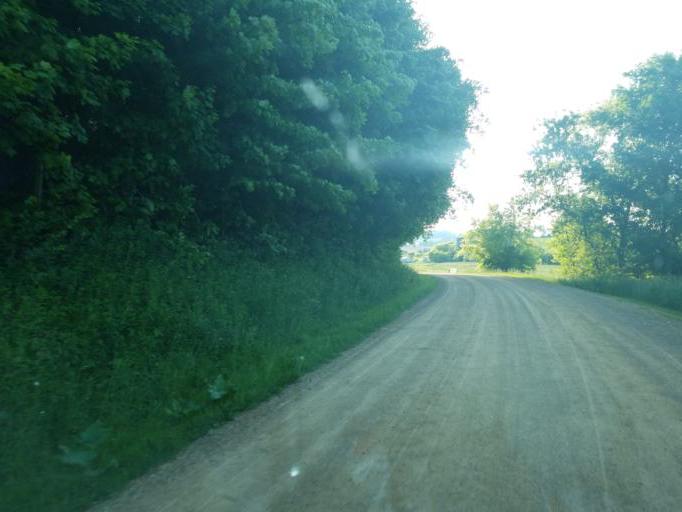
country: US
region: Wisconsin
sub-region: Vernon County
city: Hillsboro
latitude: 43.6298
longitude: -90.3420
